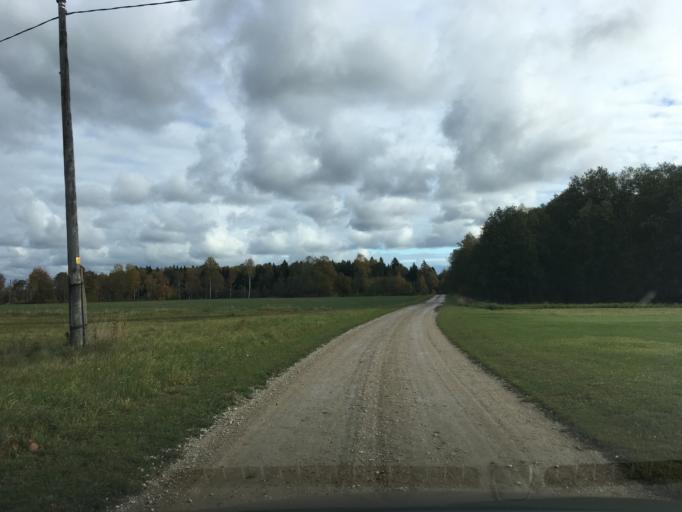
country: EE
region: Harju
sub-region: Raasiku vald
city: Raasiku
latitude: 59.2159
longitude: 25.2158
